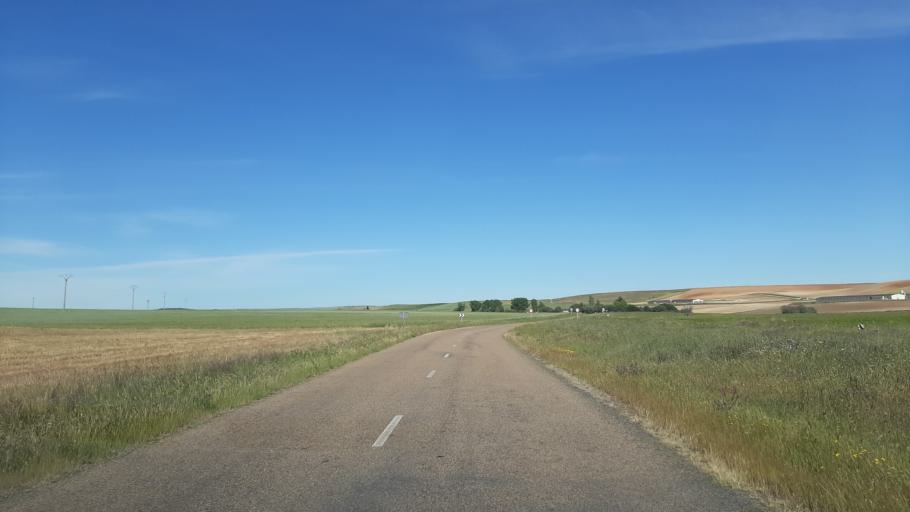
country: ES
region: Castille and Leon
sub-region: Provincia de Salamanca
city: Aldeaseca de Alba
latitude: 40.8191
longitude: -5.4719
